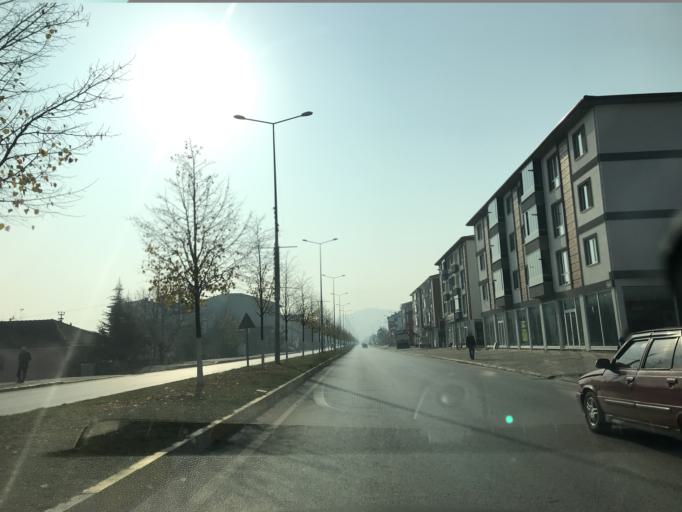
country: TR
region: Duzce
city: Cumayeri
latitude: 40.8700
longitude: 30.9515
